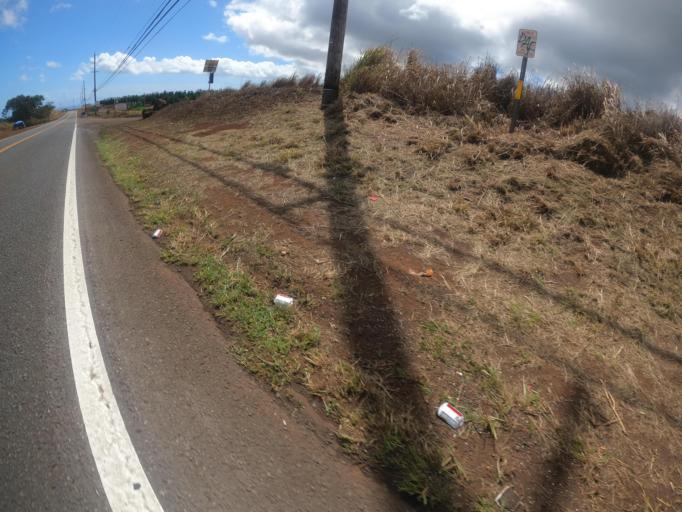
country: US
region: Hawaii
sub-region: Honolulu County
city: Village Park
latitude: 21.4308
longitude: -158.0565
